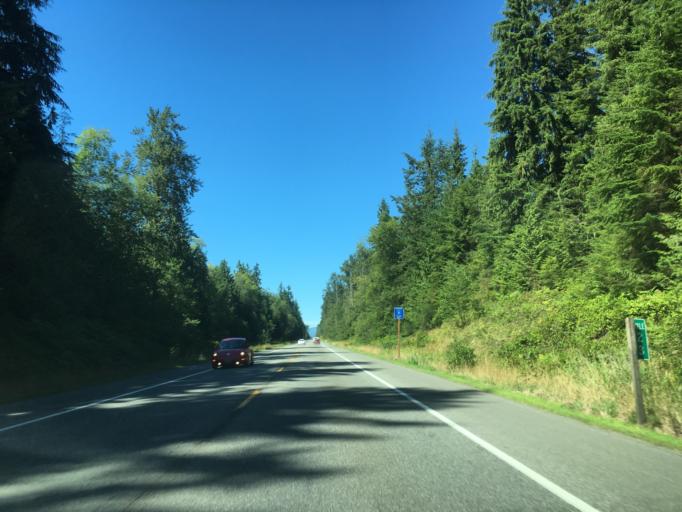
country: US
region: Washington
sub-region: Snohomish County
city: Sisco Heights
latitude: 48.1070
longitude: -122.1122
